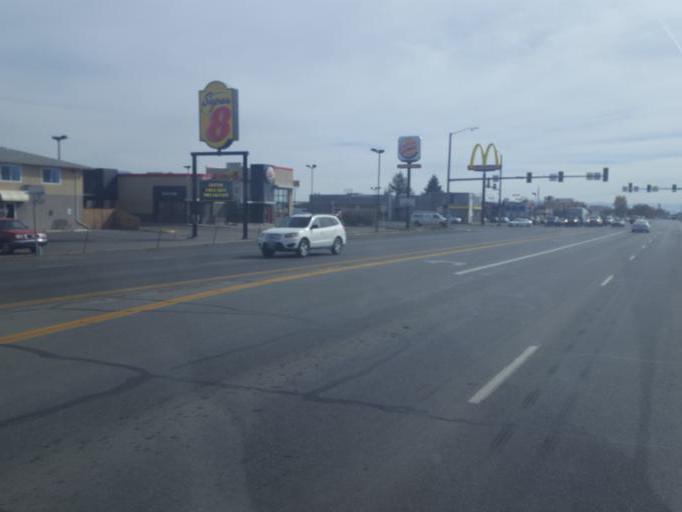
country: US
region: Colorado
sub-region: Alamosa County
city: Alamosa
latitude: 37.4756
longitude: -105.8958
